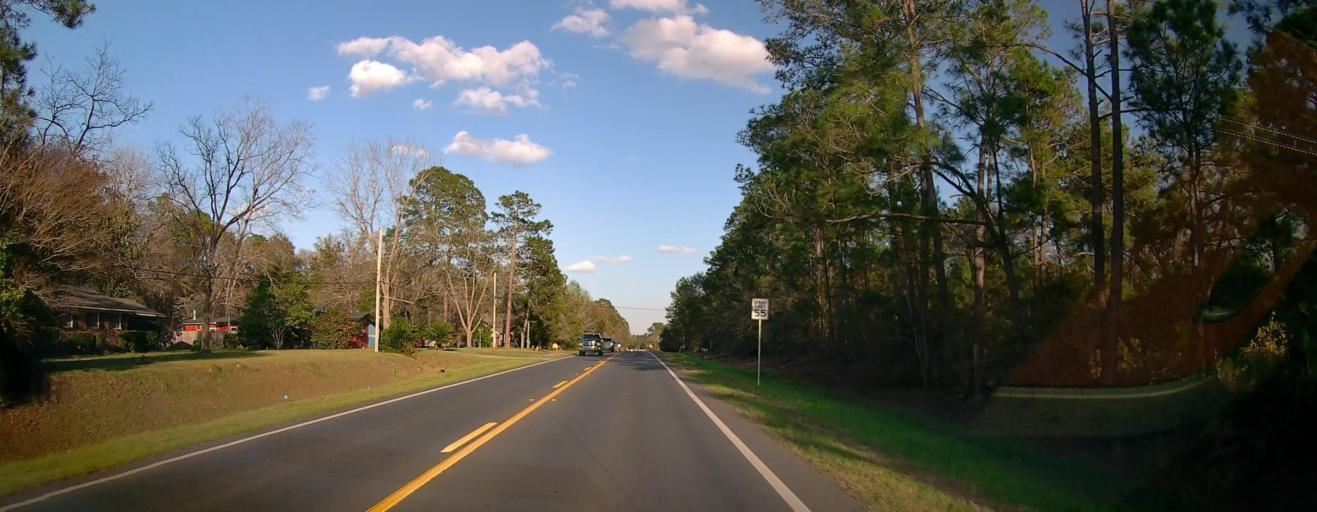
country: US
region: Georgia
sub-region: Evans County
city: Claxton
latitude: 32.1616
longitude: -81.8906
